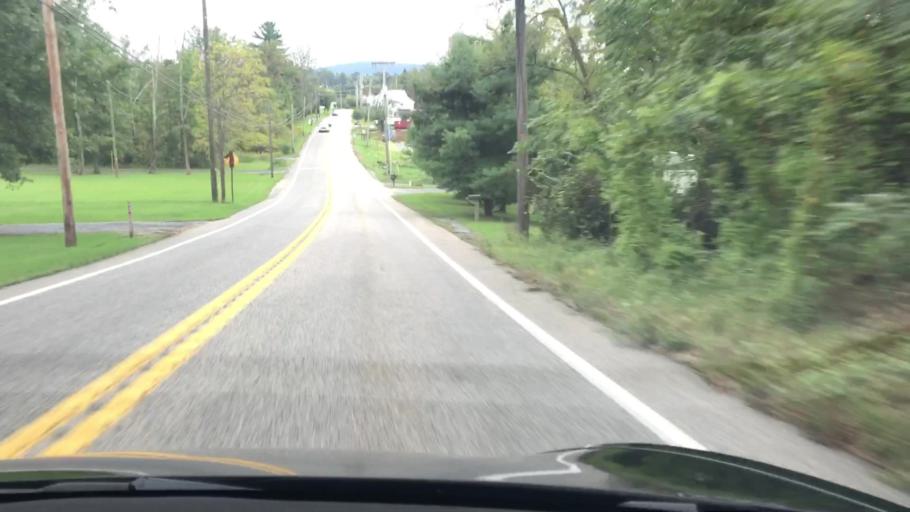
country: US
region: Pennsylvania
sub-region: Cumberland County
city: Shiremanstown
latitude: 40.1485
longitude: -76.9664
